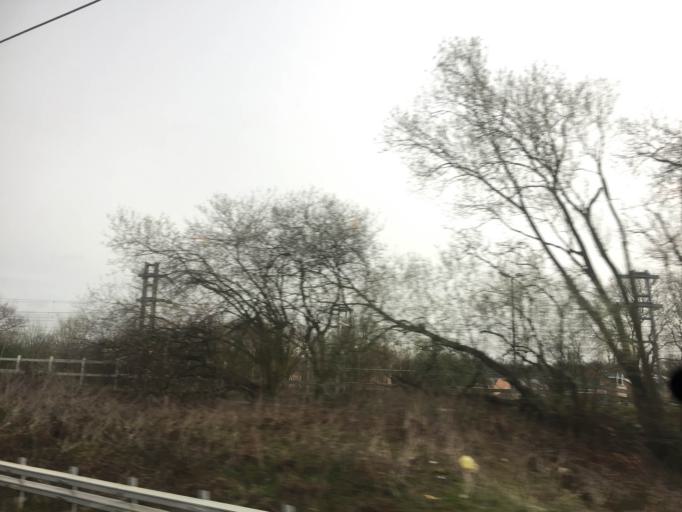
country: GB
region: England
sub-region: Lancashire
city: Euxton
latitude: 53.6766
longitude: -2.6768
